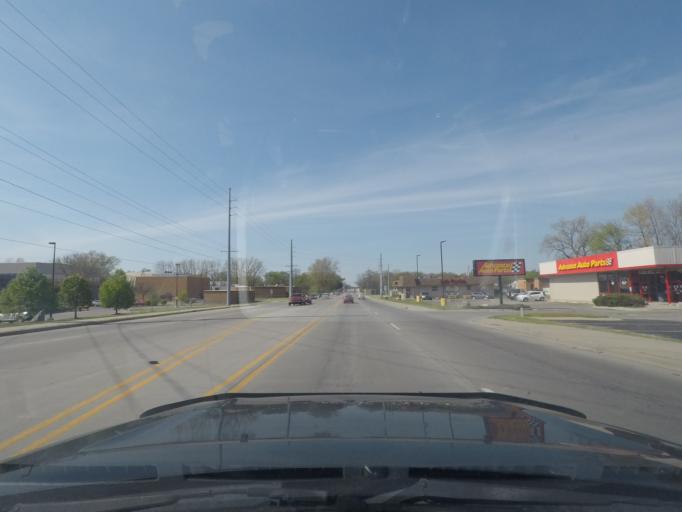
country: US
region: Indiana
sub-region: Elkhart County
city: Elkhart
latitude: 41.6761
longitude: -86.0032
